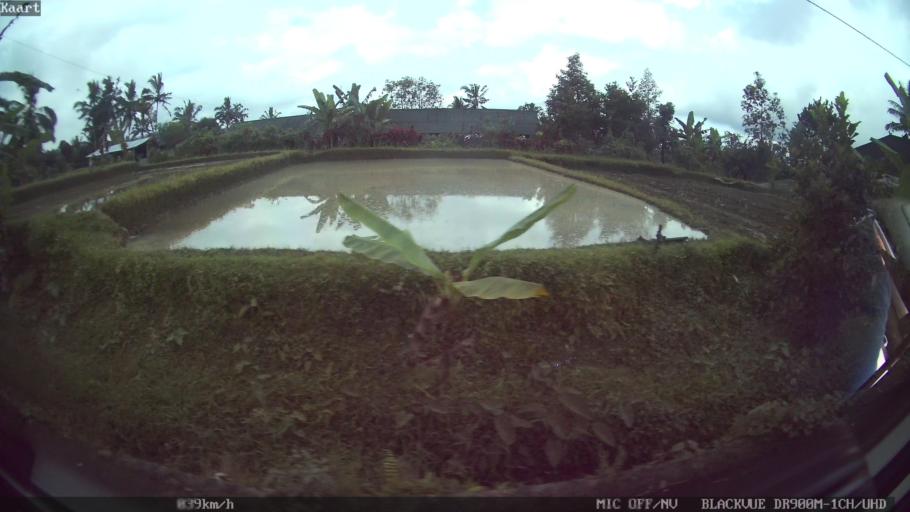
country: ID
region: Bali
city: Peneng
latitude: -8.3602
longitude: 115.1851
